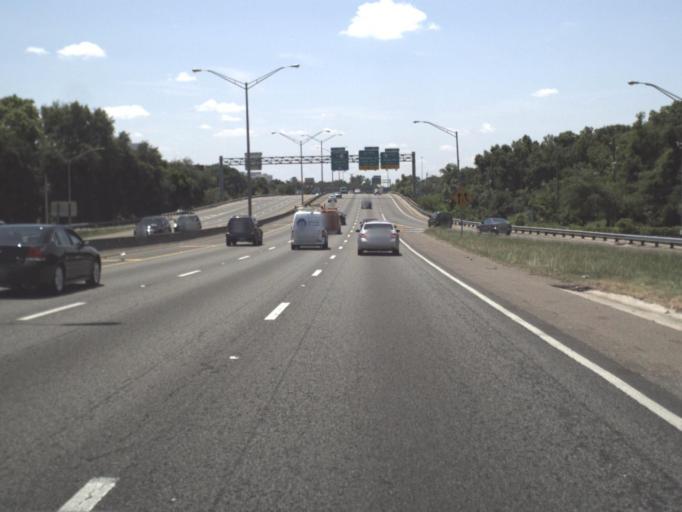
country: US
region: Florida
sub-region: Duval County
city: Jacksonville
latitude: 30.3461
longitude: -81.6684
